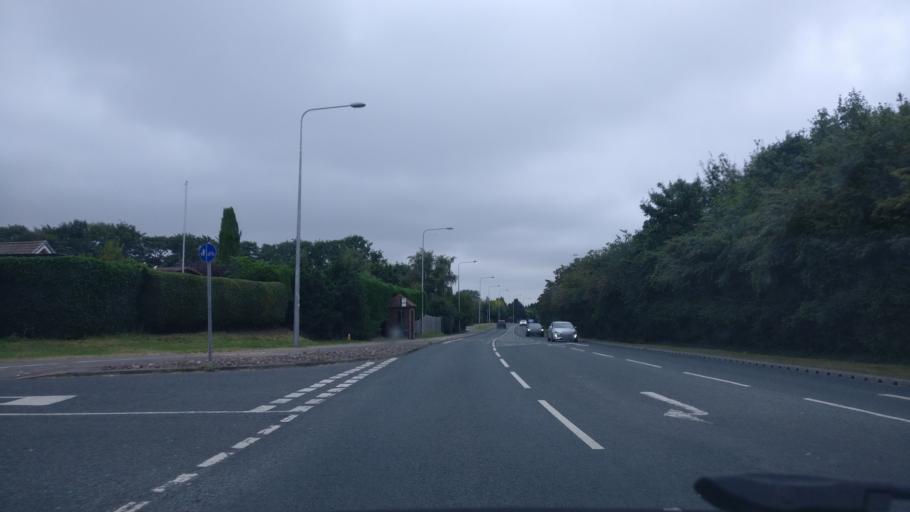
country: GB
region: England
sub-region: East Riding of Yorkshire
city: Beverley
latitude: 53.8273
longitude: -0.4400
